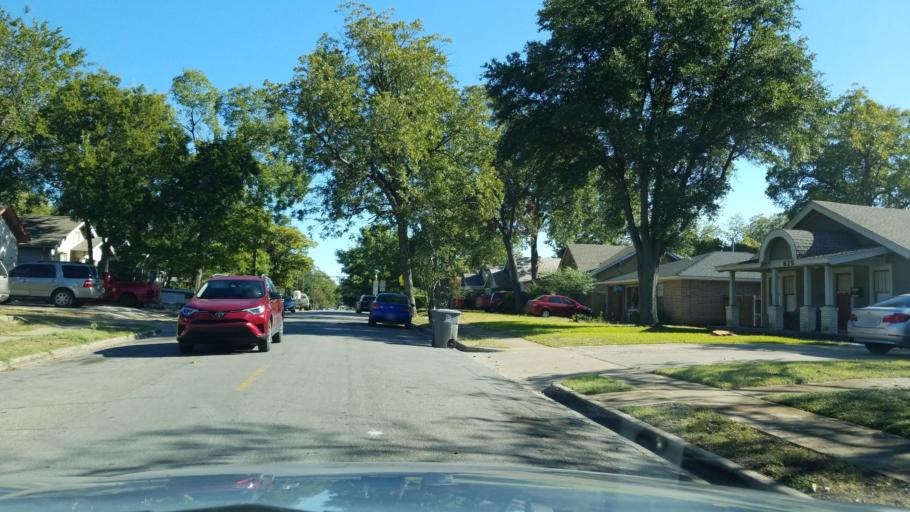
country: US
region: Texas
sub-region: Dallas County
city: Highland Park
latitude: 32.7976
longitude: -96.7486
